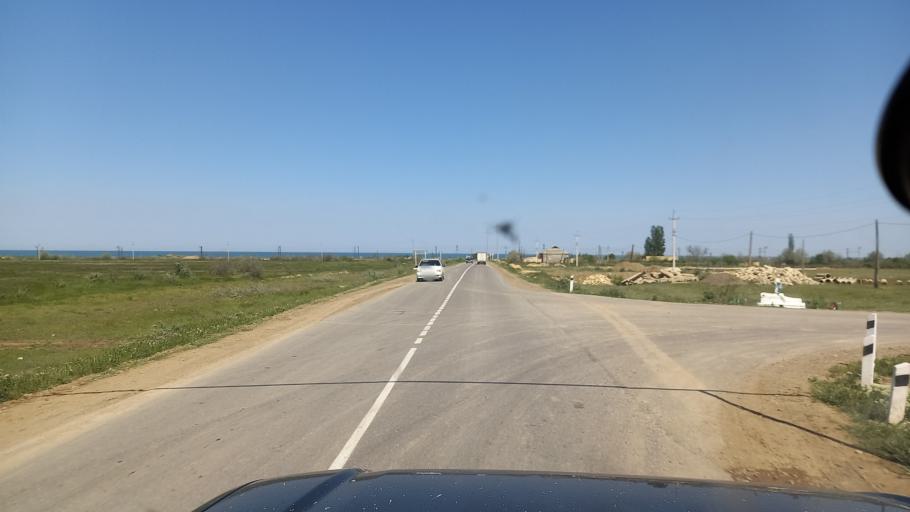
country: RU
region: Dagestan
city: Khazar
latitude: 41.9430
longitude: 48.3389
